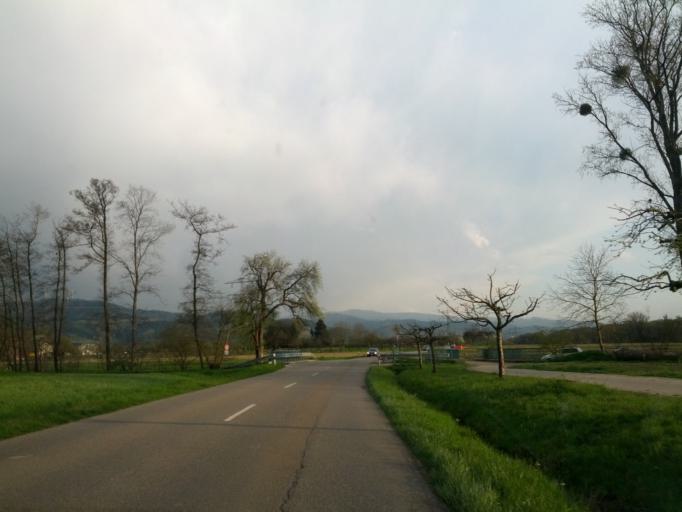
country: DE
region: Baden-Wuerttemberg
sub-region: Freiburg Region
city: Vorstetten
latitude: 48.0570
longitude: 7.8551
